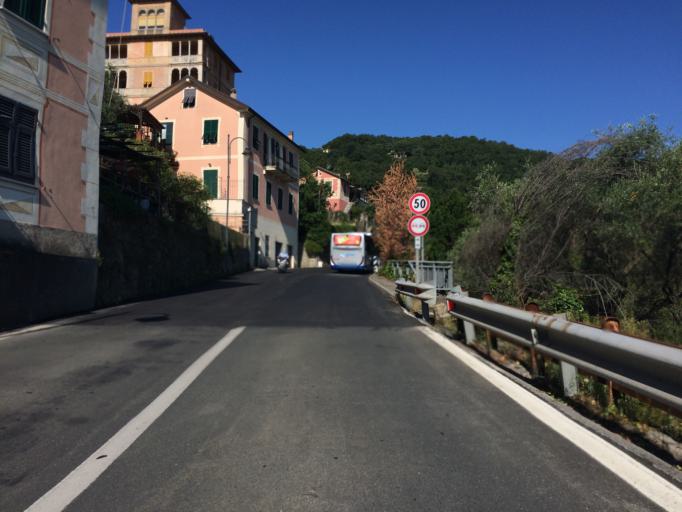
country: IT
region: Liguria
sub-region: Provincia di Genova
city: Santa Margherita Ligure
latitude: 44.3391
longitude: 9.1859
